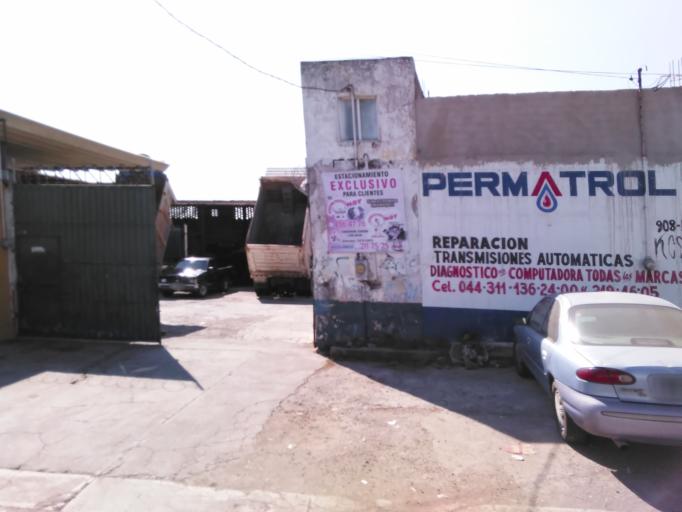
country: MX
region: Nayarit
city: Xalisco
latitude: 21.4753
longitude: -104.8630
